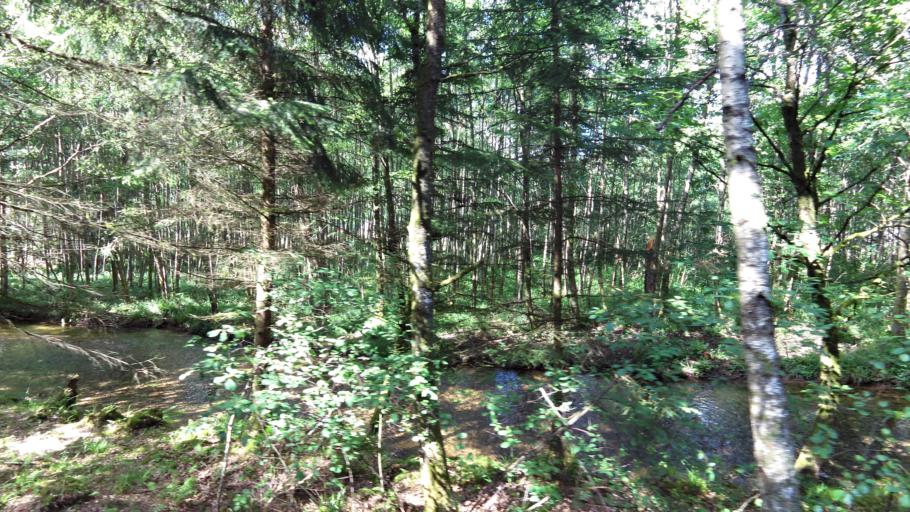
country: FR
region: Lorraine
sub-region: Departement de la Moselle
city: Abreschviller
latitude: 48.6274
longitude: 7.1166
